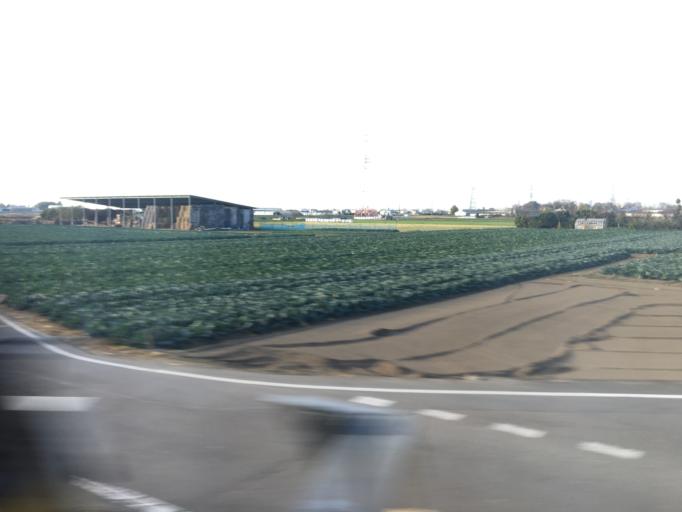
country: JP
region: Gunma
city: Omamacho-omama
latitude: 36.3665
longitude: 139.2516
